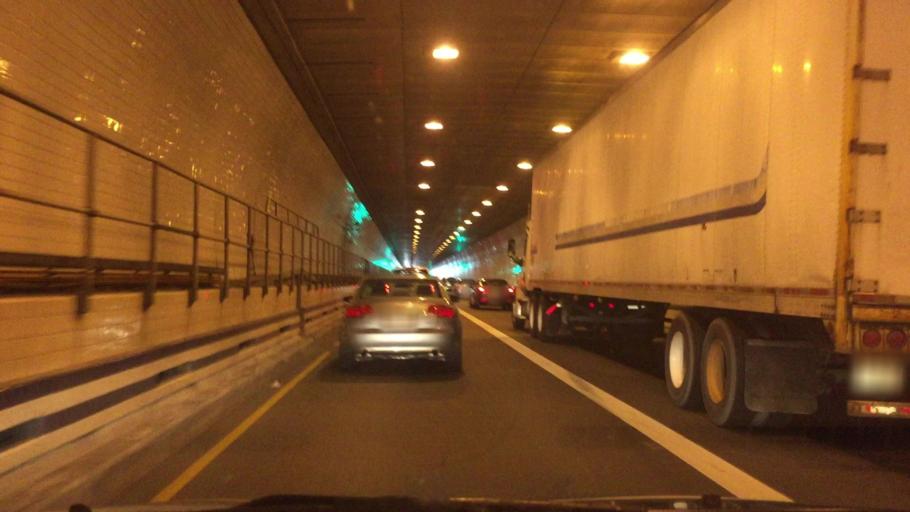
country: US
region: Virginia
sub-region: City of Newport News
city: Newport News
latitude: 36.9525
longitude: -76.4069
